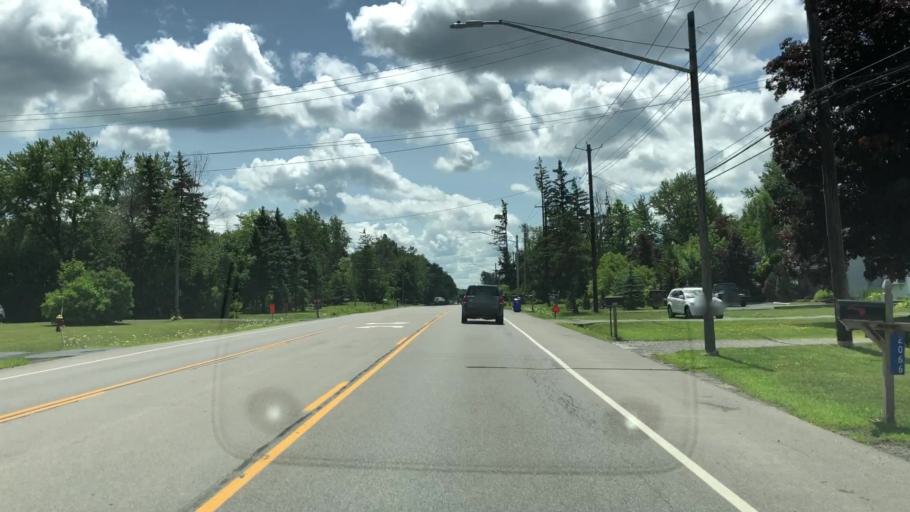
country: US
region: New York
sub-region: Erie County
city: Elma Center
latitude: 42.8237
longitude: -78.6970
